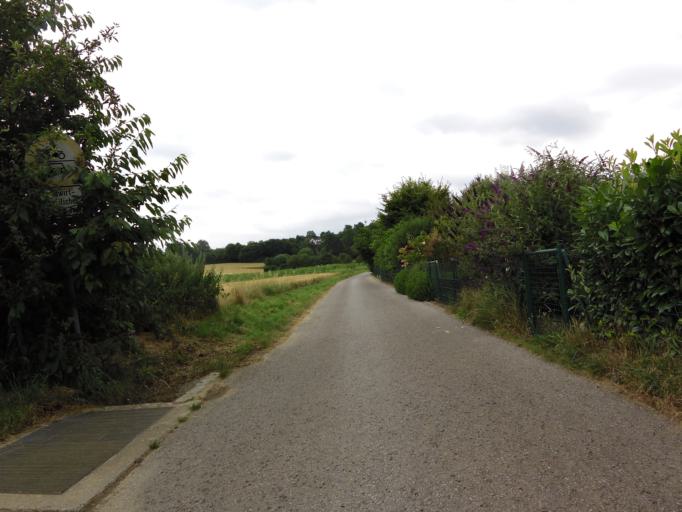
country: DE
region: Bavaria
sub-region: Regierungsbezirk Unterfranken
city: Reichenberg
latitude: 49.7580
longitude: 9.9359
